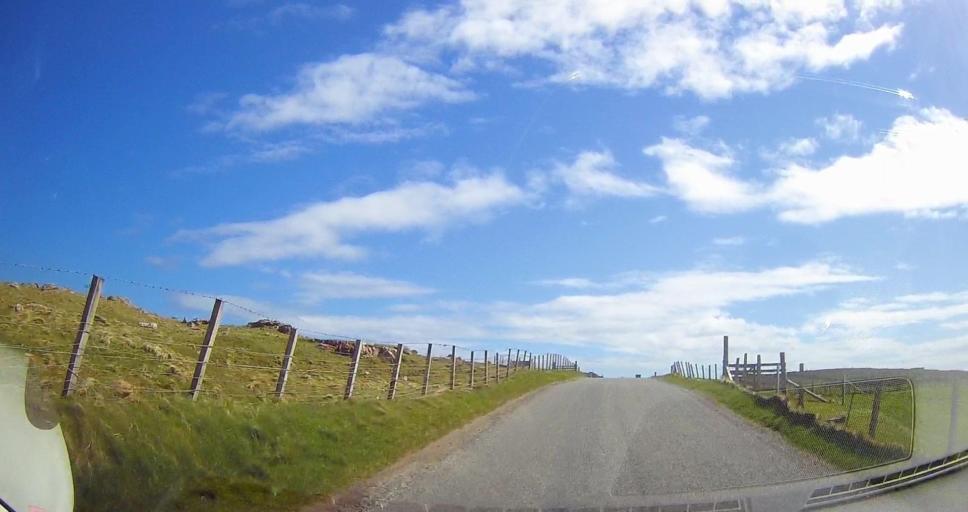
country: GB
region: Scotland
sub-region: Shetland Islands
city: Sandwick
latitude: 59.9390
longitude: -1.3226
